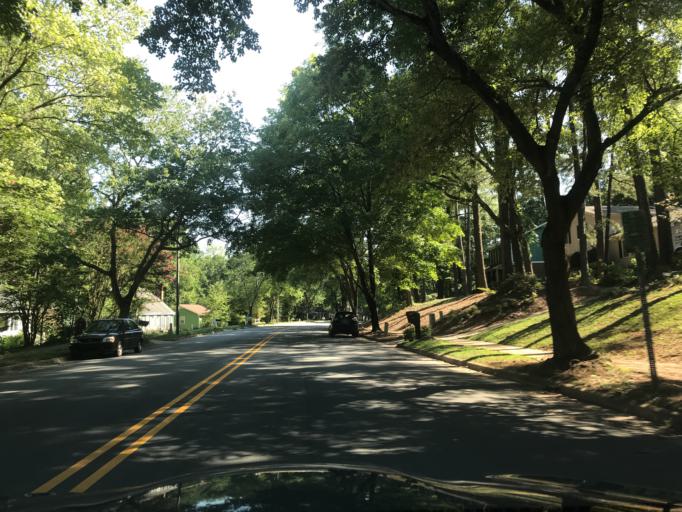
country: US
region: North Carolina
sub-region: Wake County
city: West Raleigh
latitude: 35.8605
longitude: -78.6057
